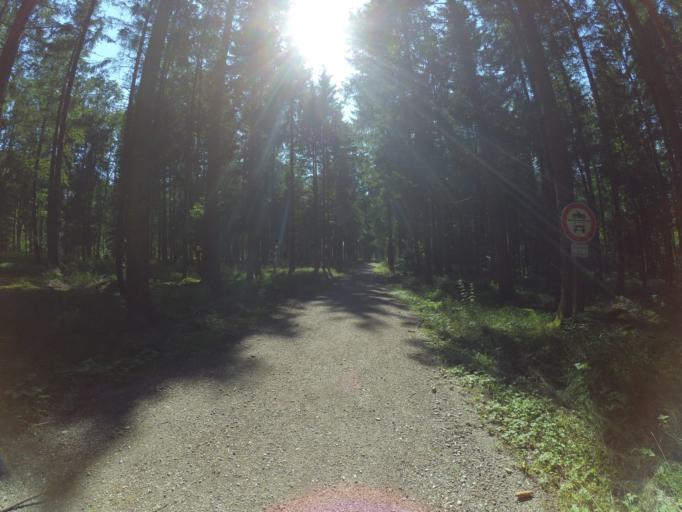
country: DE
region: Bavaria
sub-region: Swabia
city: Bad Worishofen
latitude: 47.9882
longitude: 10.5721
